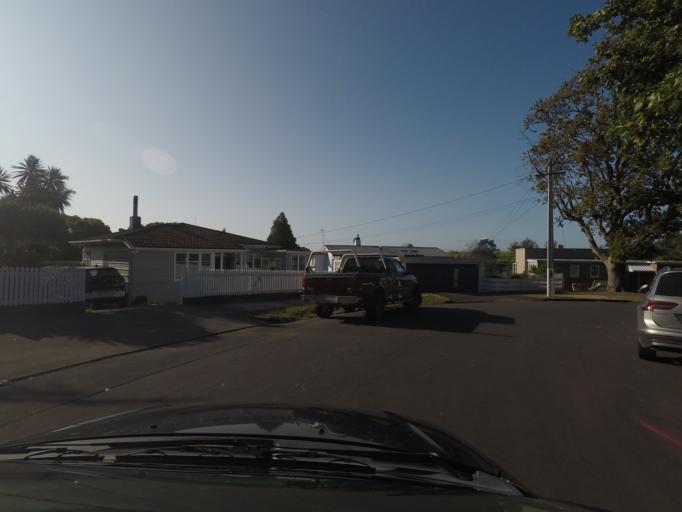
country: NZ
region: Auckland
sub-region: Auckland
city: Rosebank
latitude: -36.8632
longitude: 174.7132
